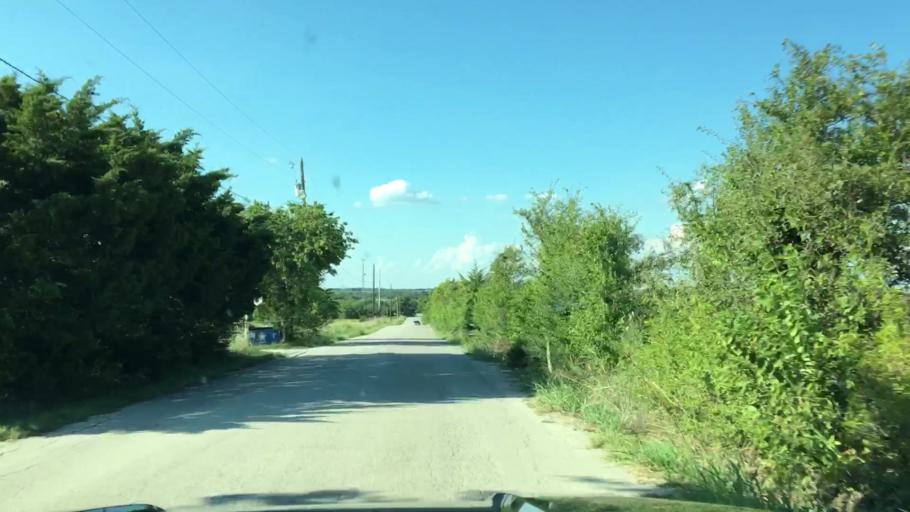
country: US
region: Texas
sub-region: Tarrant County
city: Haslet
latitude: 33.0248
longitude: -97.3767
